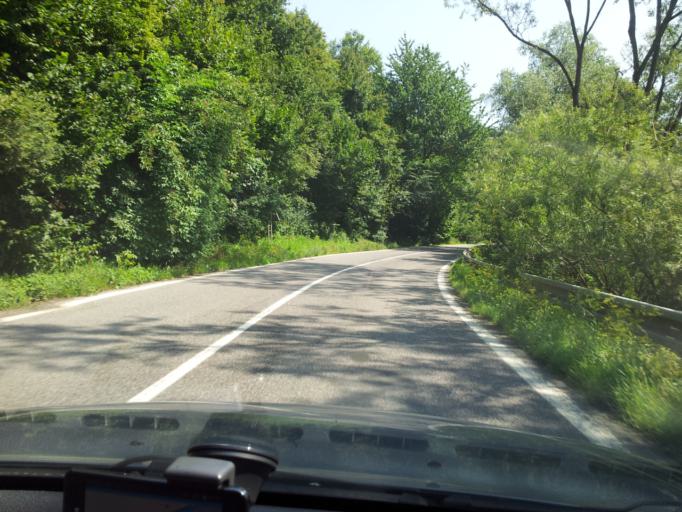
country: SK
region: Zilinsky
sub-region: Okres Dolny Kubin
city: Dolny Kubin
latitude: 49.2672
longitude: 19.3671
